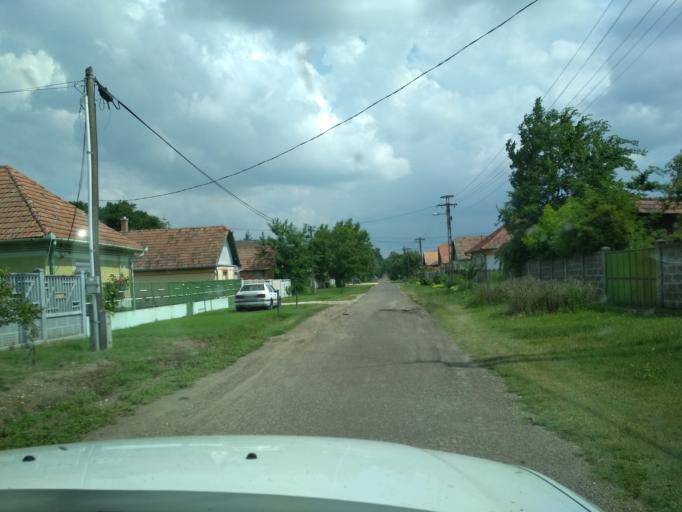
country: HU
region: Pest
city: Tapioszentmarton
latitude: 47.3335
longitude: 19.7583
